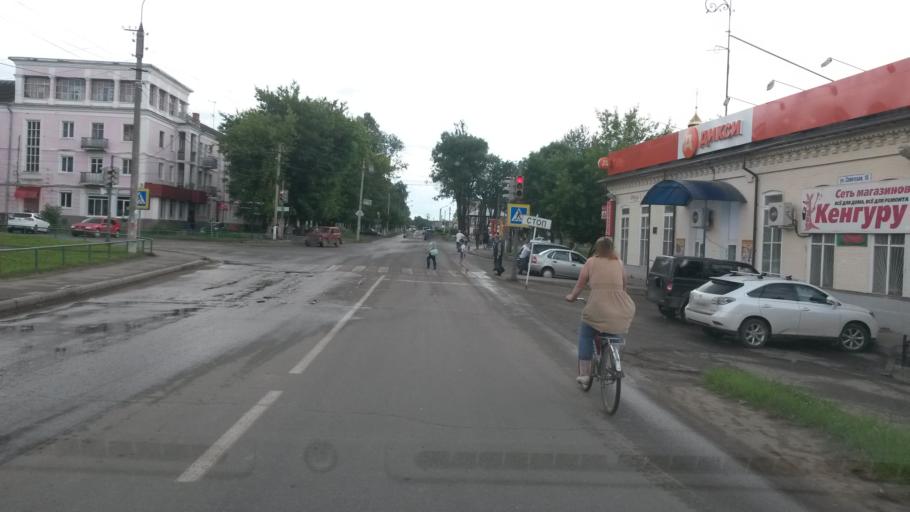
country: RU
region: Jaroslavl
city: Gavrilov-Yam
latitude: 57.3052
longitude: 39.8532
